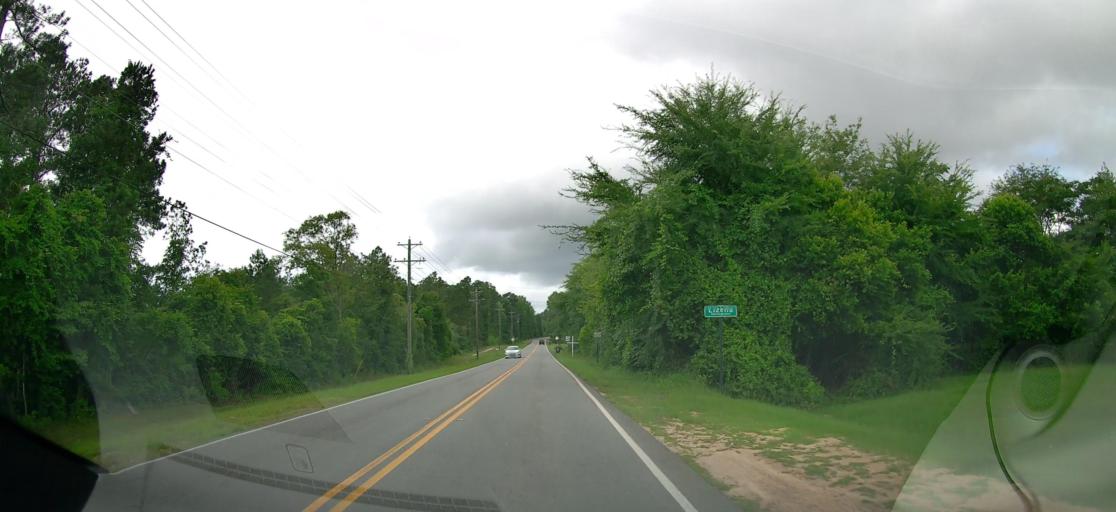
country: US
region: Georgia
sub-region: Bibb County
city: West Point
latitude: 32.7584
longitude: -83.7620
